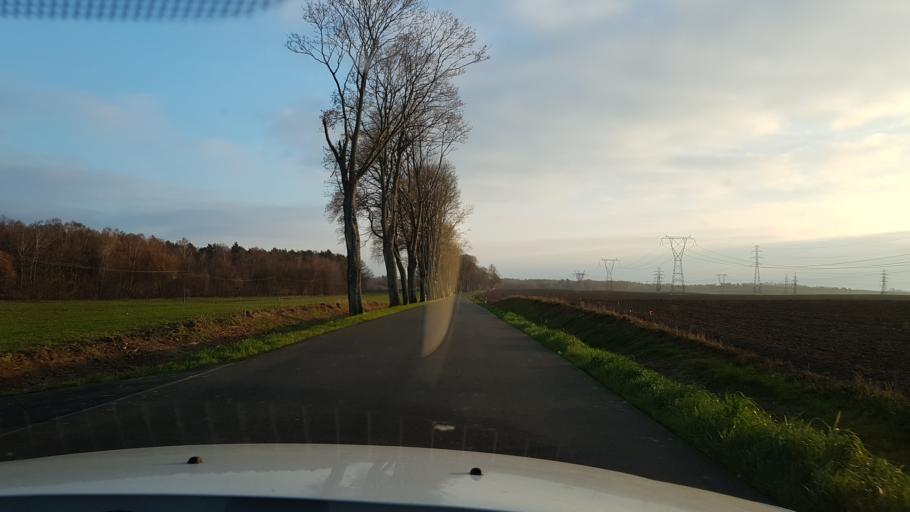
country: PL
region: West Pomeranian Voivodeship
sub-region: Koszalin
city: Koszalin
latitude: 54.1347
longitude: 16.0843
